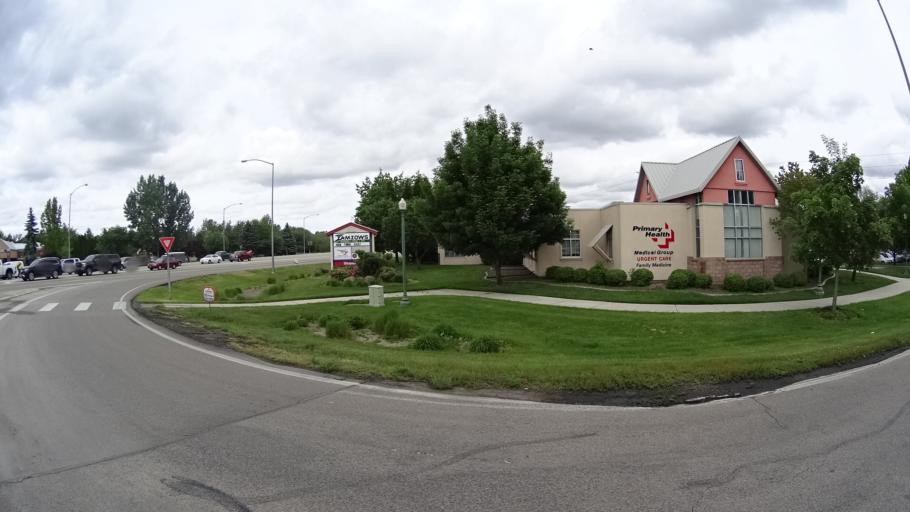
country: US
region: Idaho
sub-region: Ada County
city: Eagle
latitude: 43.6913
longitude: -116.3541
